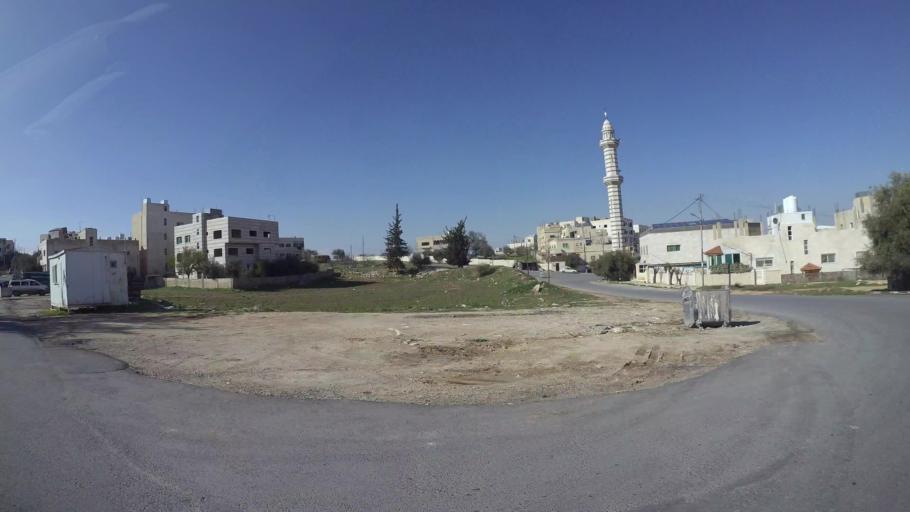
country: JO
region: Amman
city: Al Bunayyat ash Shamaliyah
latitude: 31.9067
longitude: 35.9098
